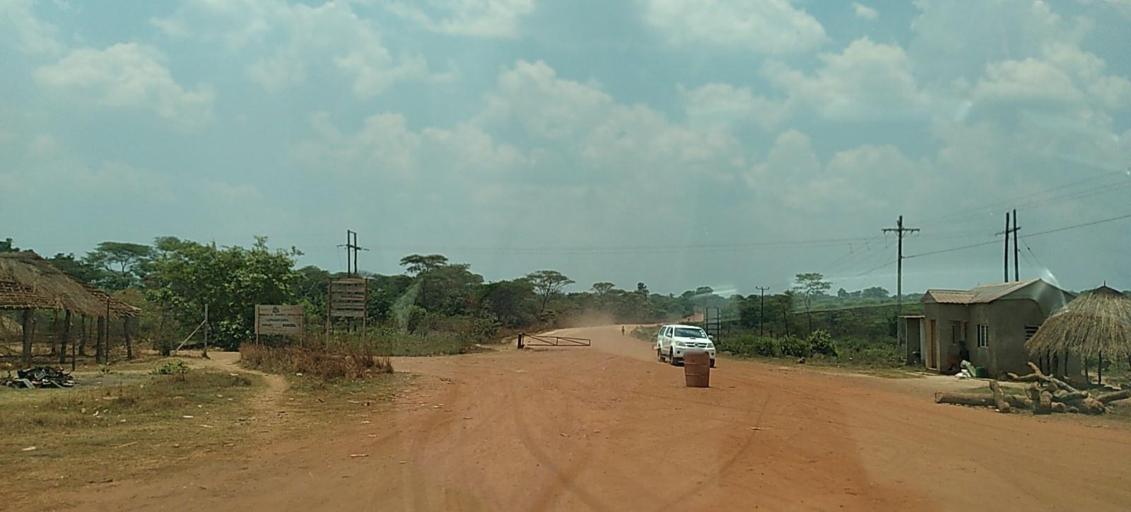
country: ZM
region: Copperbelt
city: Chingola
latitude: -12.8692
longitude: 27.6001
